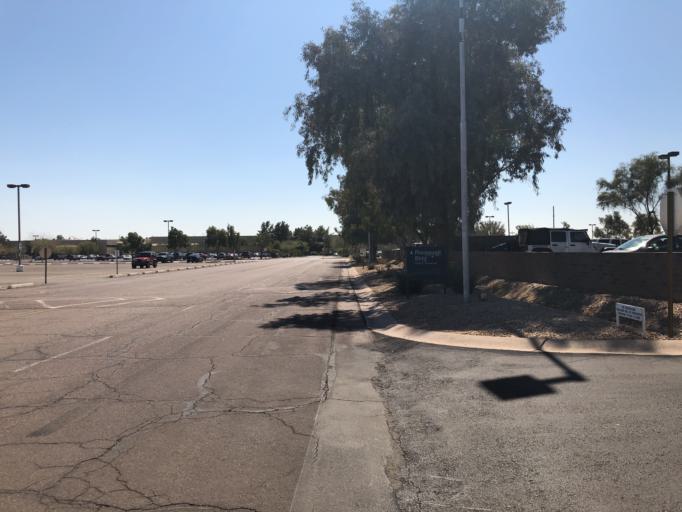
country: US
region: Arizona
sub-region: Maricopa County
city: Scottsdale
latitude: 33.4633
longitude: -111.9063
